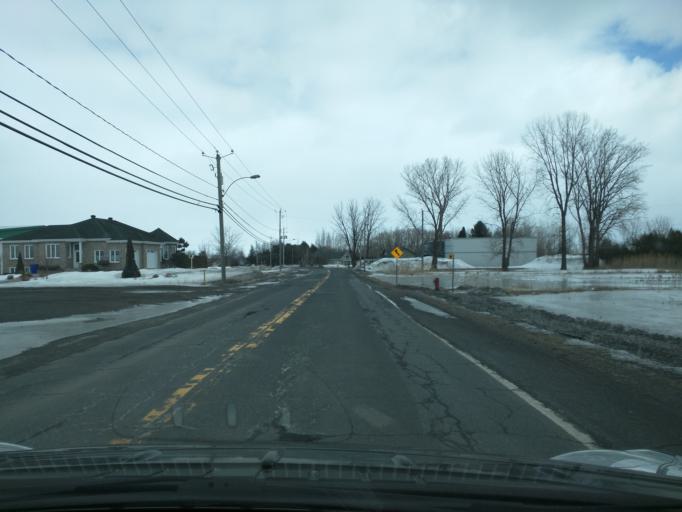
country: CA
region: Quebec
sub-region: Monteregie
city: Sainte-Julie
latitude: 45.6610
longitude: -73.2869
